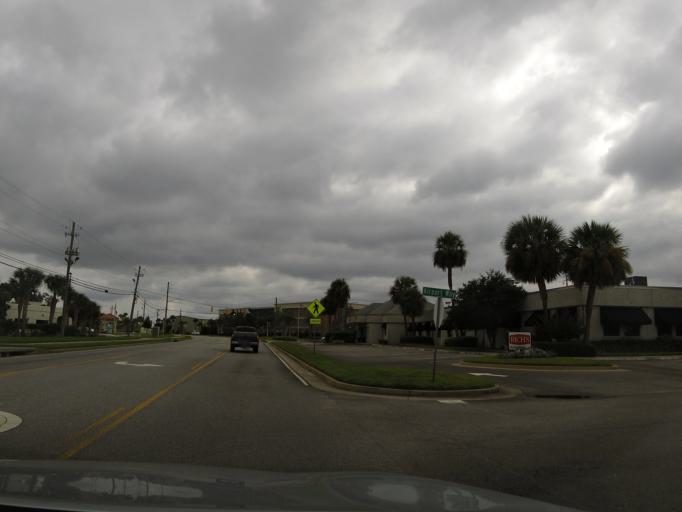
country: US
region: Georgia
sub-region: Glynn County
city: Saint Simons Island
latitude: 31.1567
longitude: -81.3860
